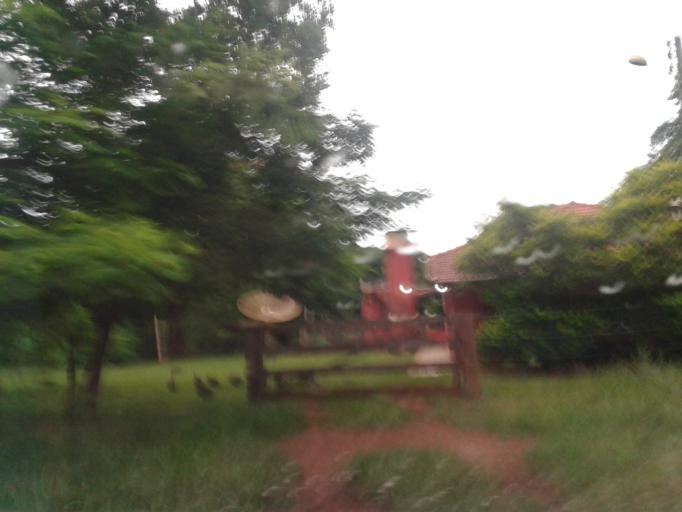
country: BR
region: Minas Gerais
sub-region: Santa Vitoria
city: Santa Vitoria
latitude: -19.2295
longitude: -50.5014
